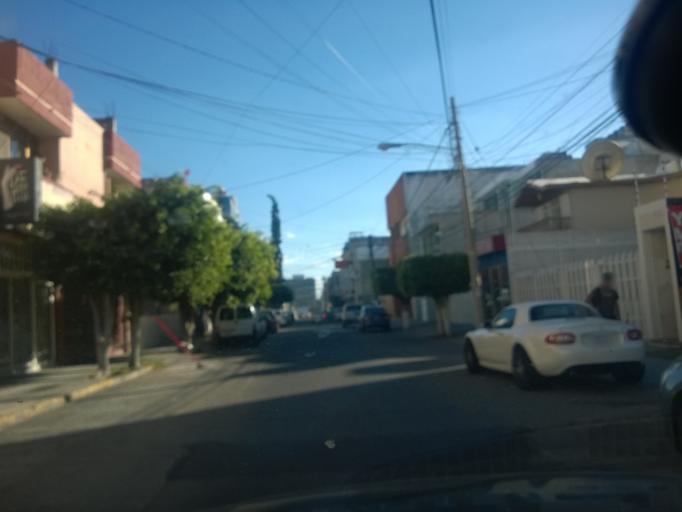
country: MX
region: Guanajuato
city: Leon
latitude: 21.1442
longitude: -101.6876
